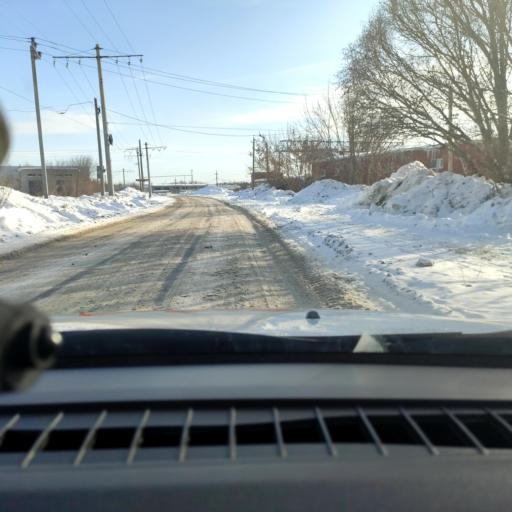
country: RU
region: Samara
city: Smyshlyayevka
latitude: 53.2577
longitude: 50.3635
